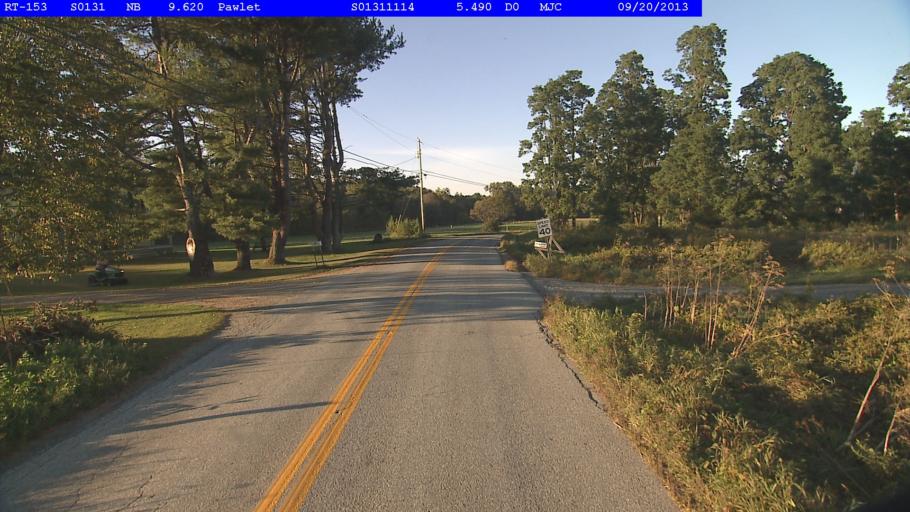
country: US
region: New York
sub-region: Washington County
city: Granville
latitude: 43.3829
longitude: -73.2268
